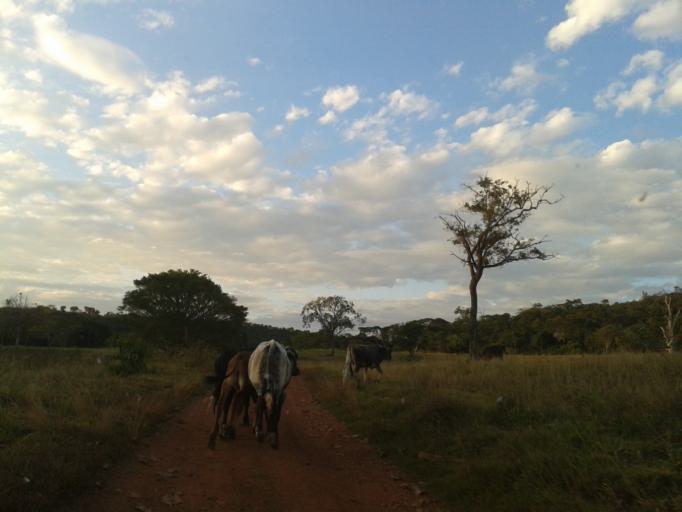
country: BR
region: Minas Gerais
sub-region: Campina Verde
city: Campina Verde
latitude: -19.3505
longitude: -49.6676
